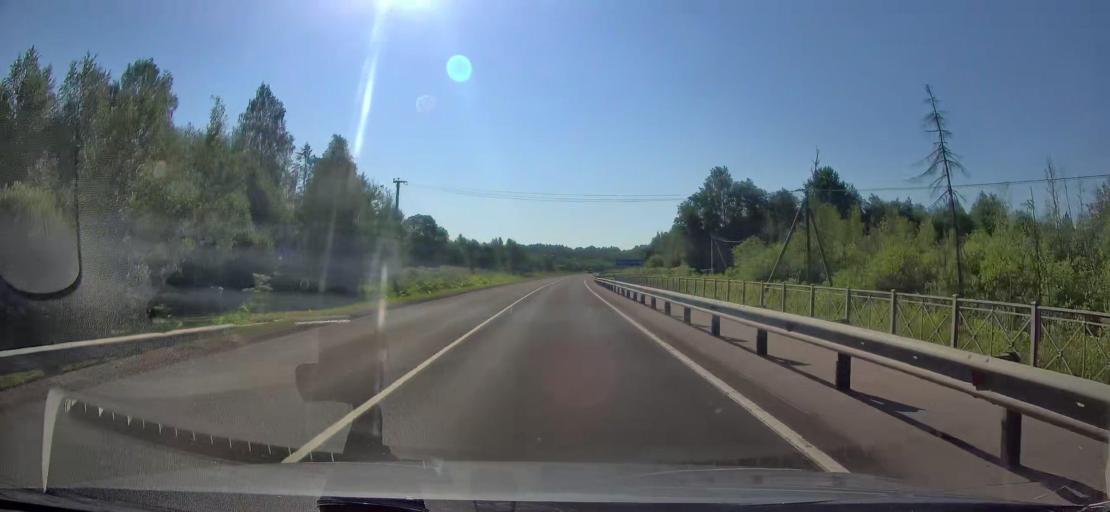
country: RU
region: Leningrad
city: Khvalovo
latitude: 59.8770
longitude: 32.8643
